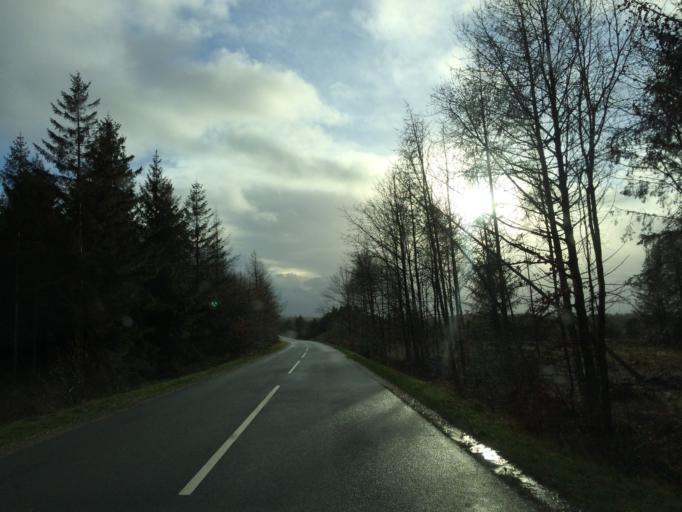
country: DK
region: Central Jutland
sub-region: Holstebro Kommune
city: Ulfborg
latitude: 56.2230
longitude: 8.3849
